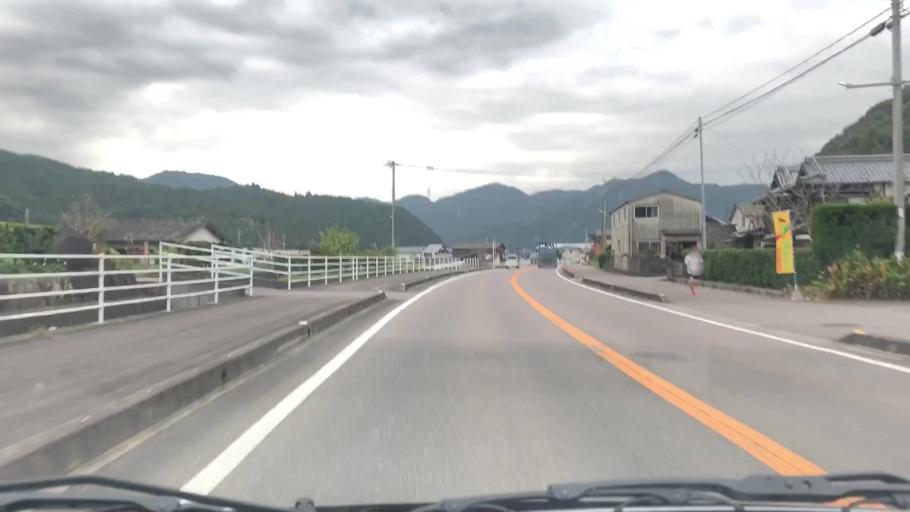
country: JP
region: Saga Prefecture
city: Kashima
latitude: 33.1278
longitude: 130.0500
